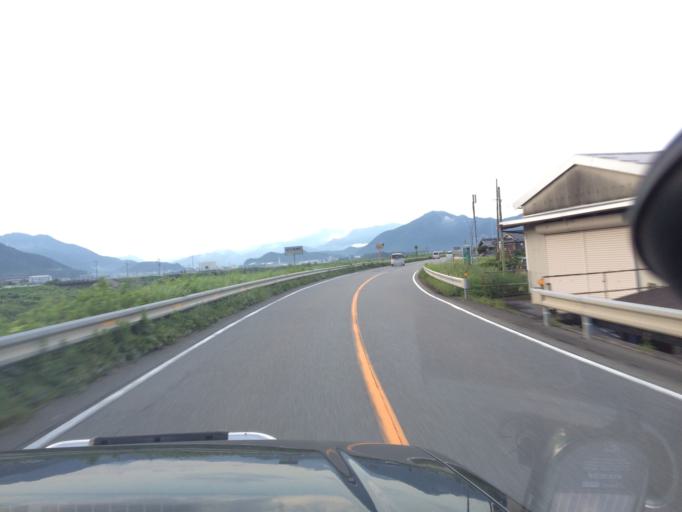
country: JP
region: Hyogo
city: Nishiwaki
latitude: 35.1415
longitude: 135.0285
